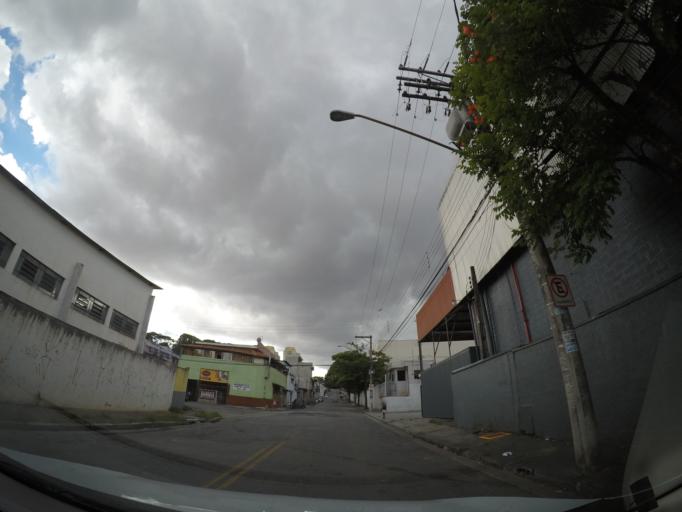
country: BR
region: Sao Paulo
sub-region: Guarulhos
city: Guarulhos
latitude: -23.4845
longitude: -46.5472
